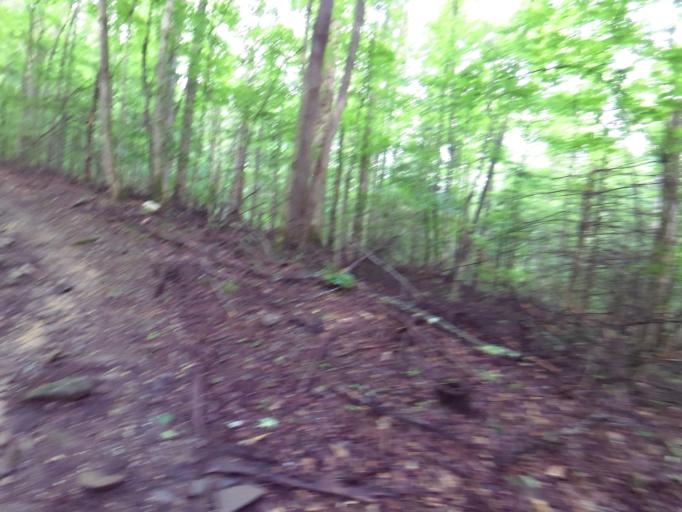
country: US
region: Tennessee
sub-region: Blount County
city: Wildwood
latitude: 35.6037
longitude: -83.7532
